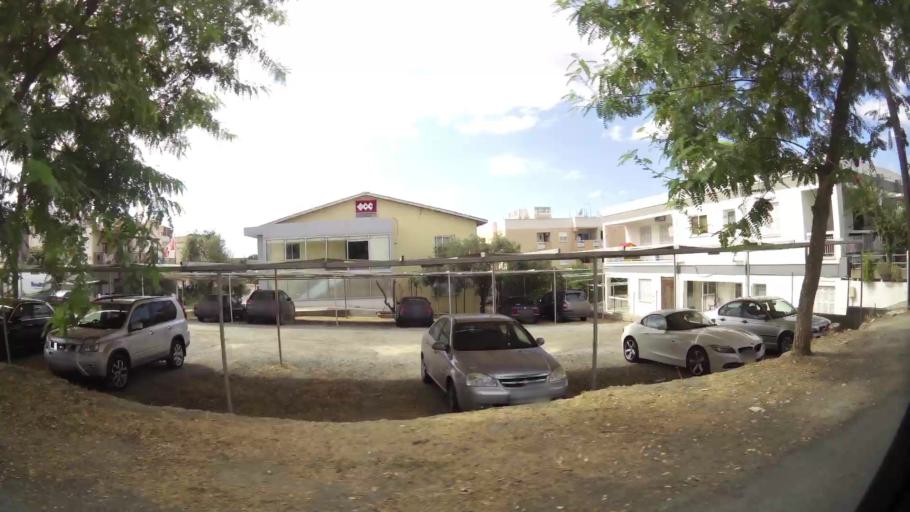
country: CY
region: Lefkosia
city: Nicosia
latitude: 35.1747
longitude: 33.3855
